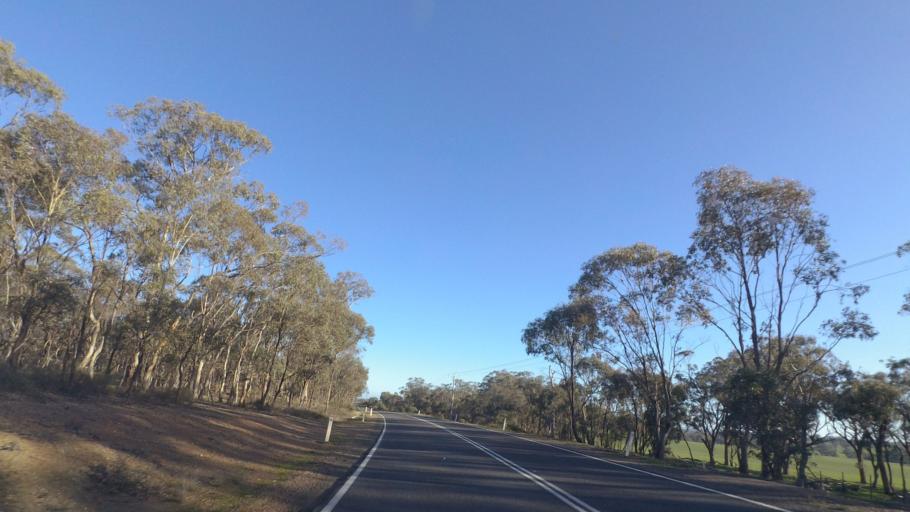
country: AU
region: Victoria
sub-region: Greater Bendigo
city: Kennington
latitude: -36.8602
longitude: 144.5036
